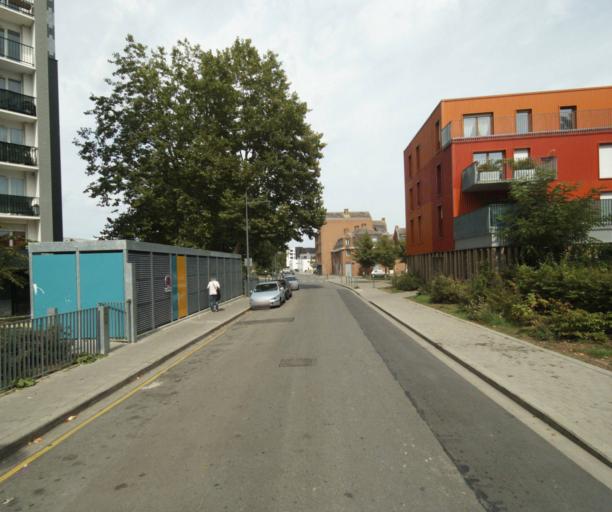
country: FR
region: Nord-Pas-de-Calais
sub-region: Departement du Nord
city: Wattignies
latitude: 50.6031
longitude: 3.0510
